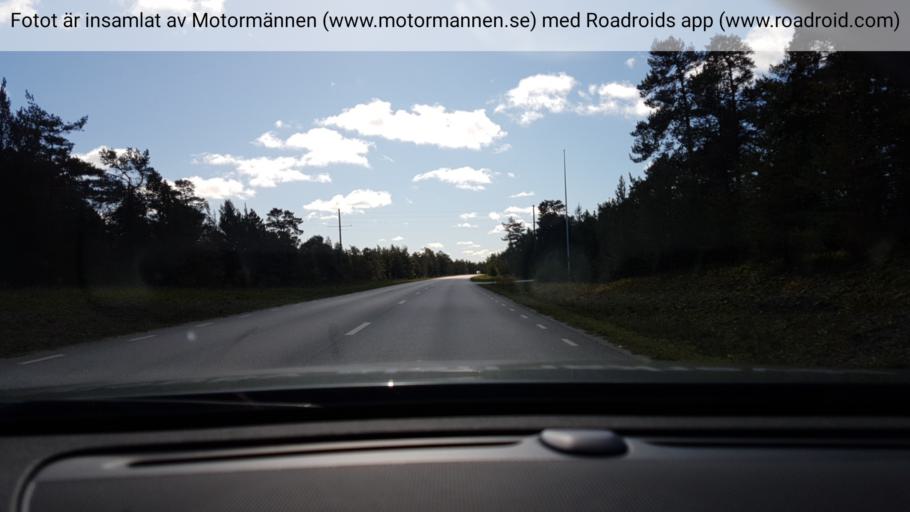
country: SE
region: Gotland
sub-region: Gotland
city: Slite
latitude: 57.7372
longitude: 18.7908
